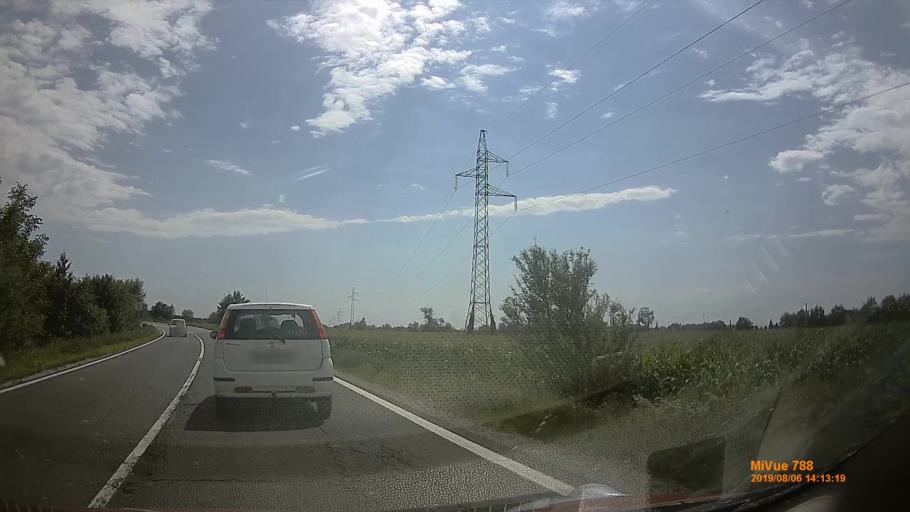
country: HU
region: Vas
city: Taplanszentkereszt
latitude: 47.2022
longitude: 16.6788
